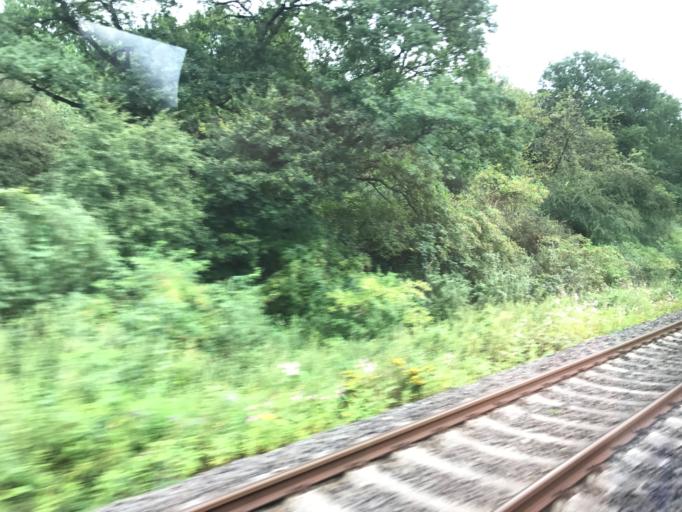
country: DE
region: Hesse
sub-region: Regierungsbezirk Giessen
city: Villmar
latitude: 50.3953
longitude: 8.1730
